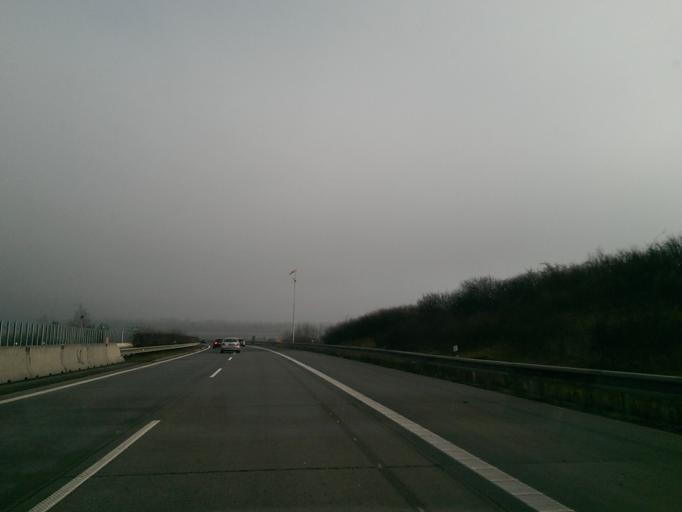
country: CZ
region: Olomoucky
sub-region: Okres Olomouc
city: Olomouc
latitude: 49.5483
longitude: 17.2437
